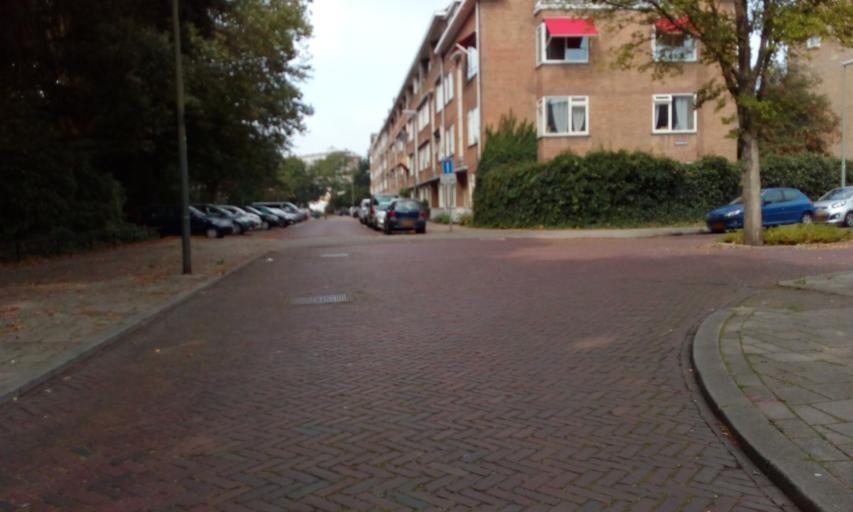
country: NL
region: South Holland
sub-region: Gemeente Schiedam
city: Schiedam
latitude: 51.9102
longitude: 4.3819
